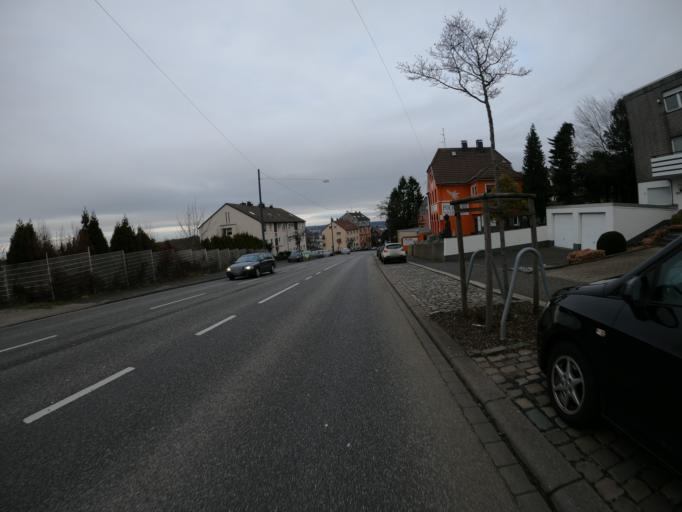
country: DE
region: North Rhine-Westphalia
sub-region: Regierungsbezirk Dusseldorf
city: Wuppertal
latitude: 51.2375
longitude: 7.1478
